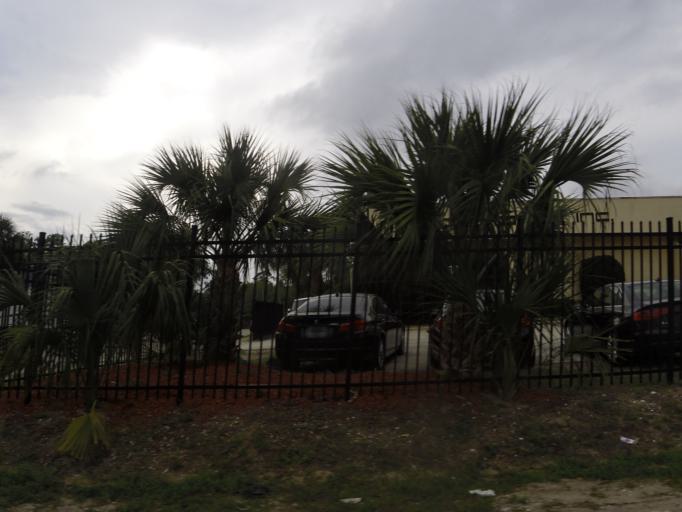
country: US
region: Florida
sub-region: Duval County
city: Jacksonville
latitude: 30.3172
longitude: -81.5602
